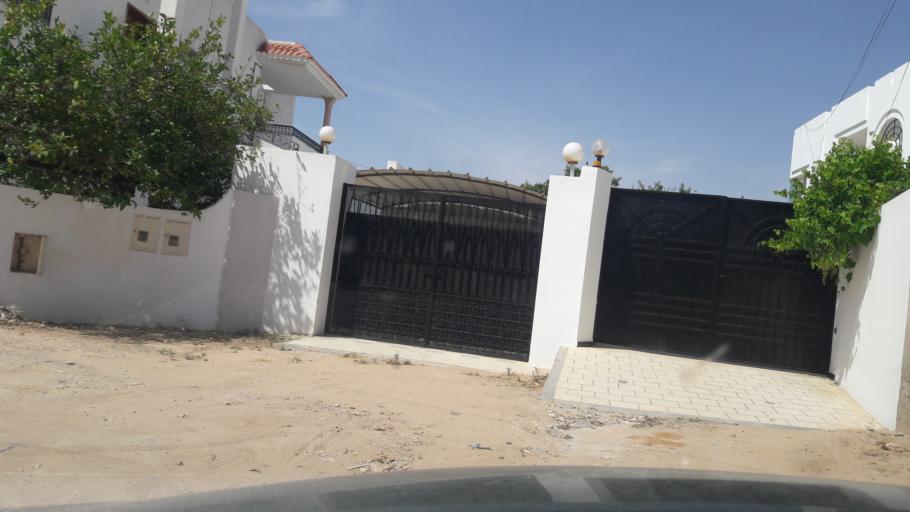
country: TN
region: Safaqis
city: Al Qarmadah
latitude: 34.7888
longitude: 10.7582
